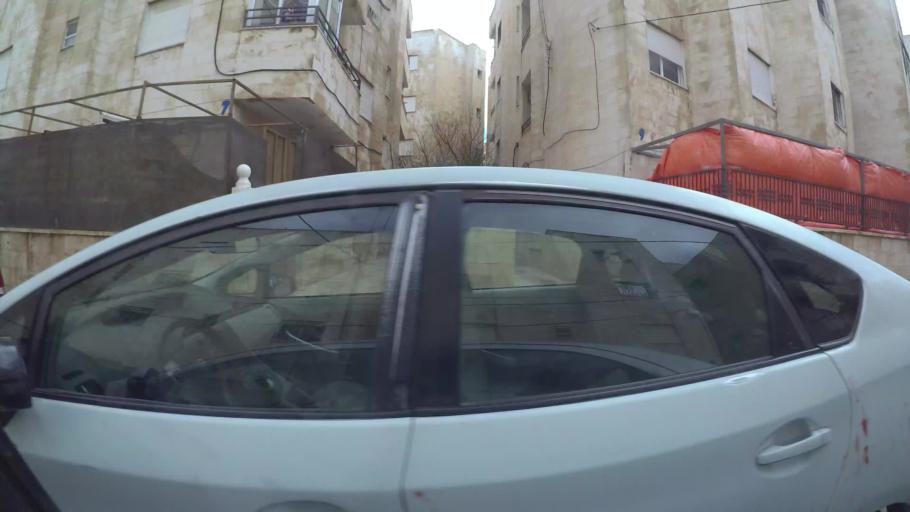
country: JO
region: Amman
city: Al Jubayhah
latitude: 32.0559
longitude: 35.8715
